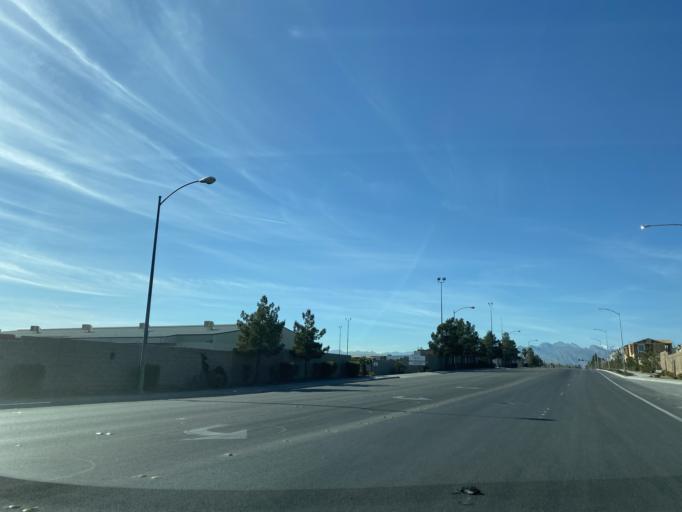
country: US
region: Nevada
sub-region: Clark County
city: North Las Vegas
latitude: 36.2250
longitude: -115.1434
